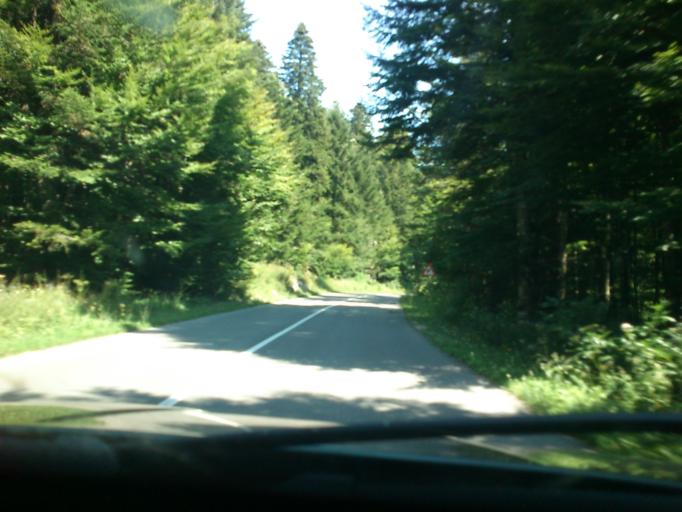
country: HR
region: Licko-Senjska
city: Senj
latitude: 44.8592
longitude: 15.0046
